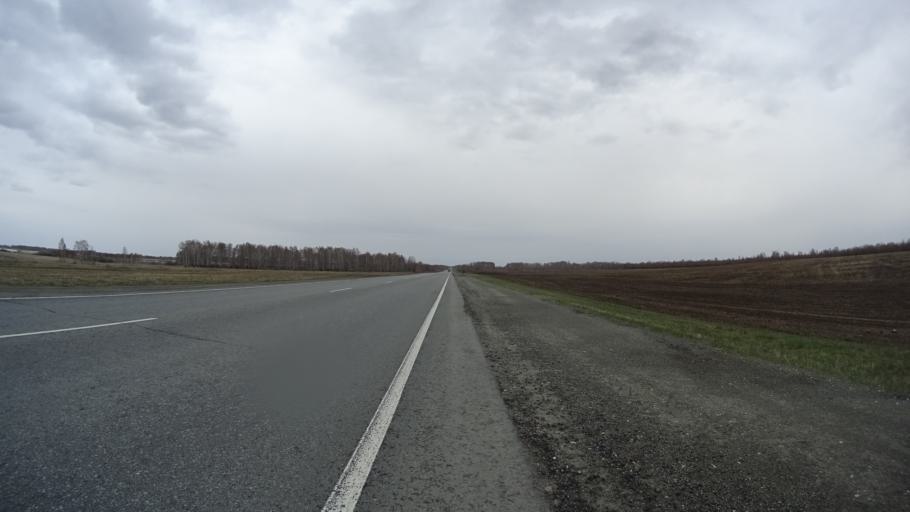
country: RU
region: Chelyabinsk
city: Krasnogorskiy
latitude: 54.6626
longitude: 61.2541
